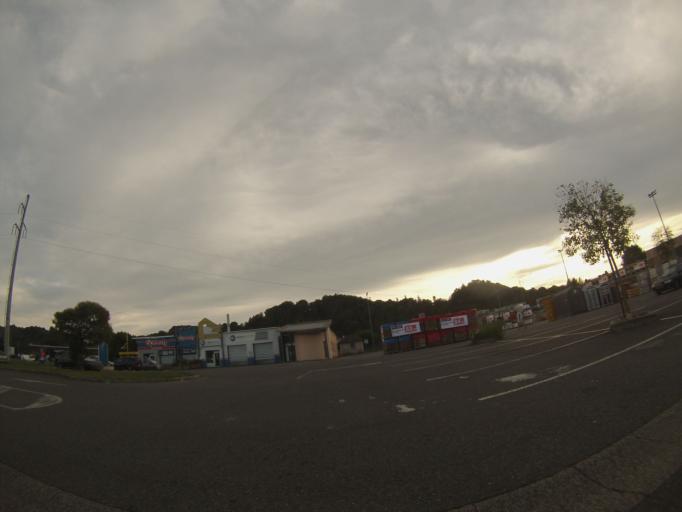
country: FR
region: Aquitaine
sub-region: Departement des Pyrenees-Atlantiques
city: Gelos
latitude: 43.2803
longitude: -0.3615
